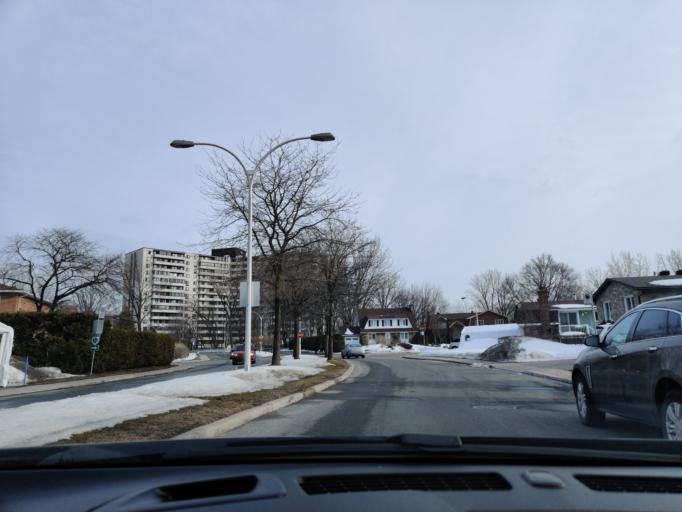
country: CA
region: Quebec
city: Dollard-Des Ormeaux
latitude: 45.5238
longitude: -73.7586
